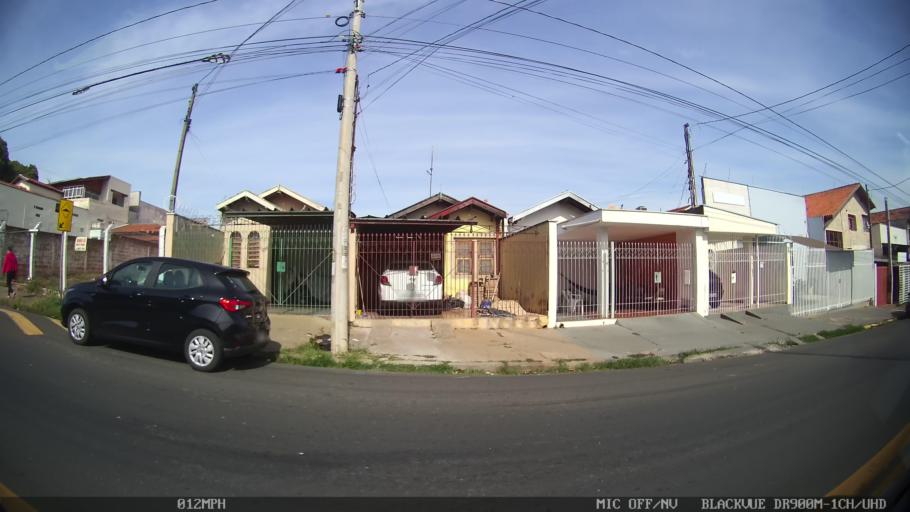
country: BR
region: Sao Paulo
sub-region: Piracicaba
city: Piracicaba
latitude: -22.7459
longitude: -47.6613
